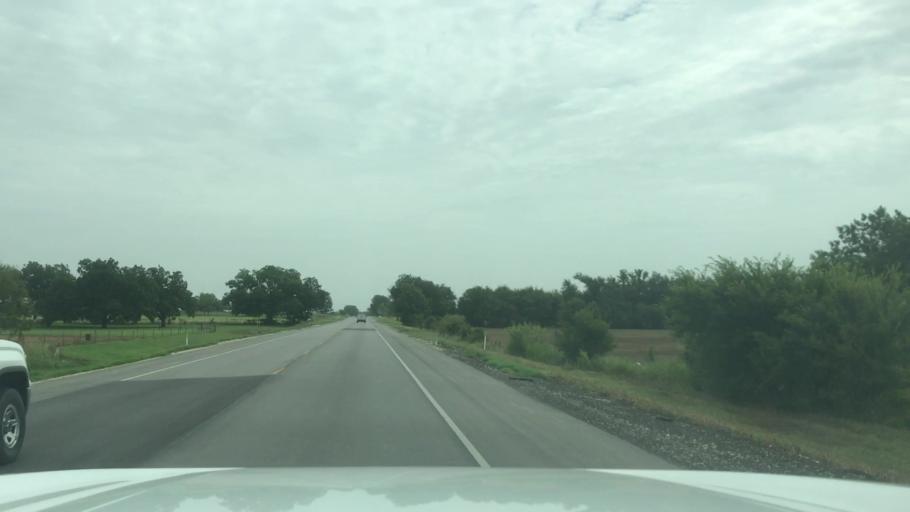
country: US
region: Texas
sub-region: Erath County
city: Dublin
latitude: 32.0896
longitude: -98.2883
